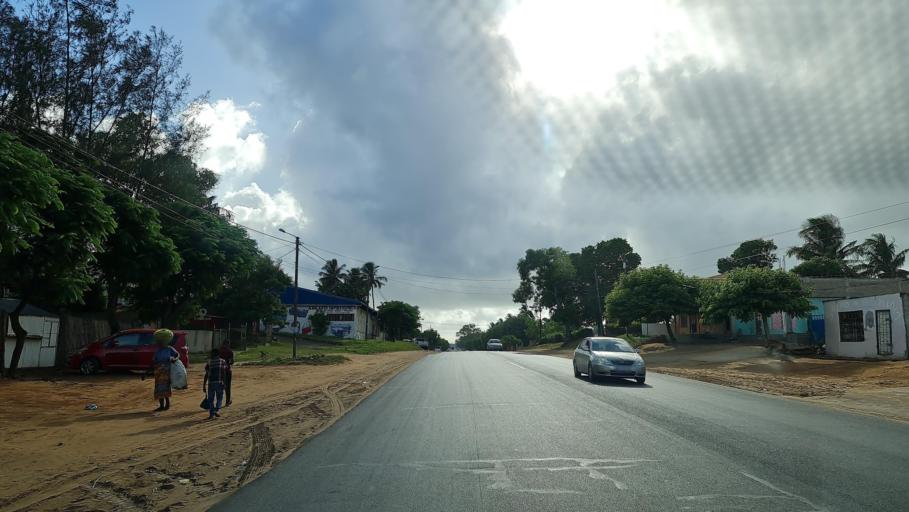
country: MZ
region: Gaza
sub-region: Xai-Xai District
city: Xai-Xai
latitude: -25.0569
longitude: 33.6827
